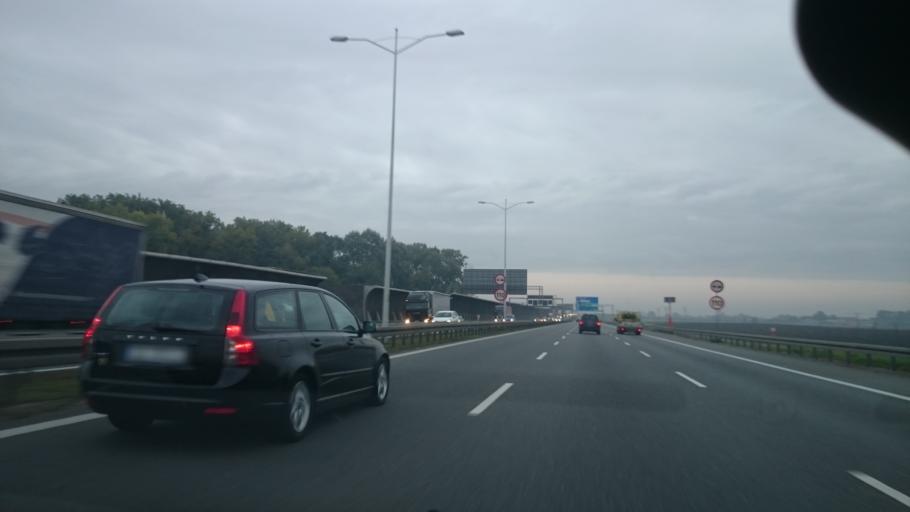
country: PL
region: Lower Silesian Voivodeship
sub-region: Powiat wroclawski
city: Tyniec Maly
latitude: 51.0568
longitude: 16.9316
